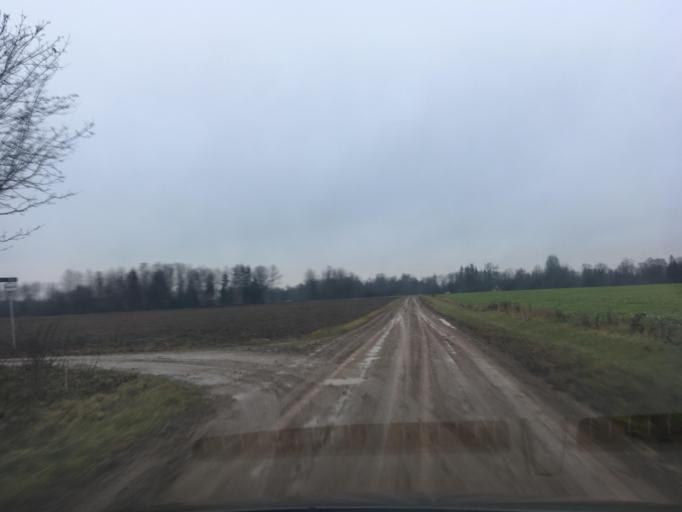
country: EE
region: Tartu
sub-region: Tartu linn
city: Tartu
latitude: 58.3902
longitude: 26.9281
